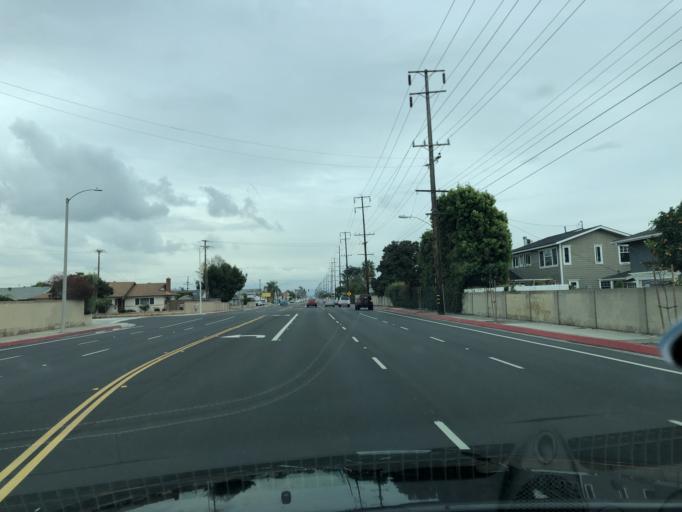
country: US
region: California
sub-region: Orange County
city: Westminster
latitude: 33.7300
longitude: -118.0189
